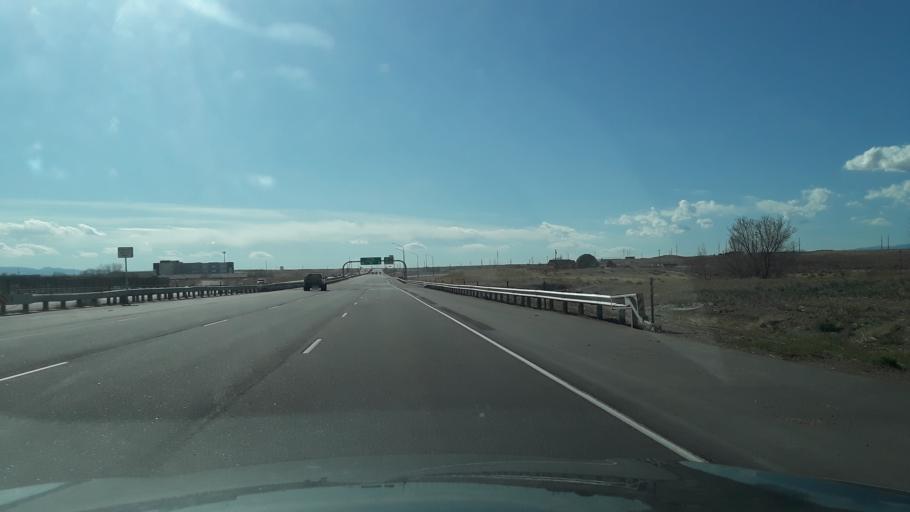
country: US
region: Colorado
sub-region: Pueblo County
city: Pueblo
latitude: 38.3127
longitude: -104.6509
